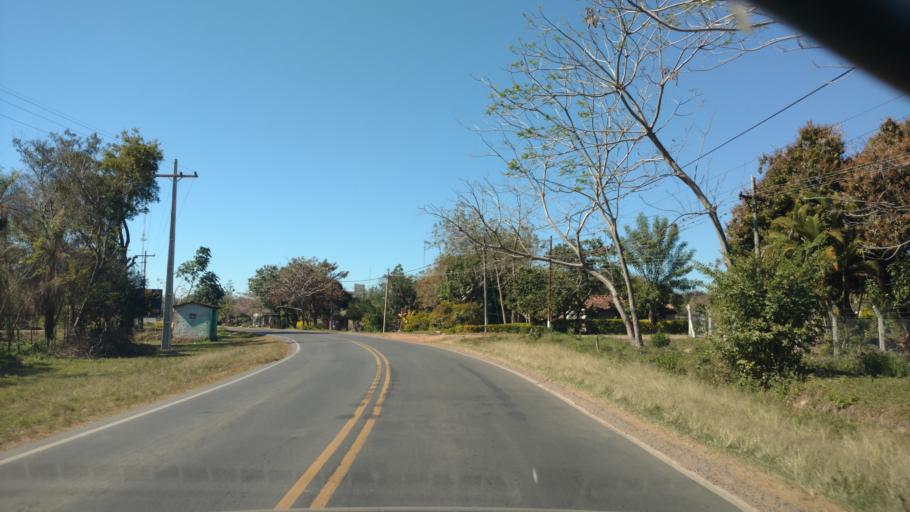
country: PY
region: Paraguari
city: Pirayu
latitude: -25.4735
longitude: -57.2531
